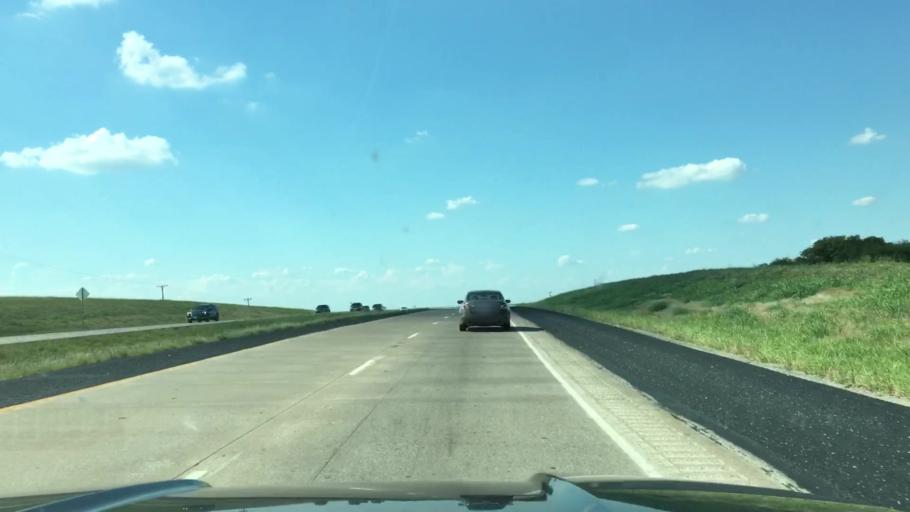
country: US
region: Texas
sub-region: Wise County
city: New Fairview
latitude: 33.1278
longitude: -97.4910
